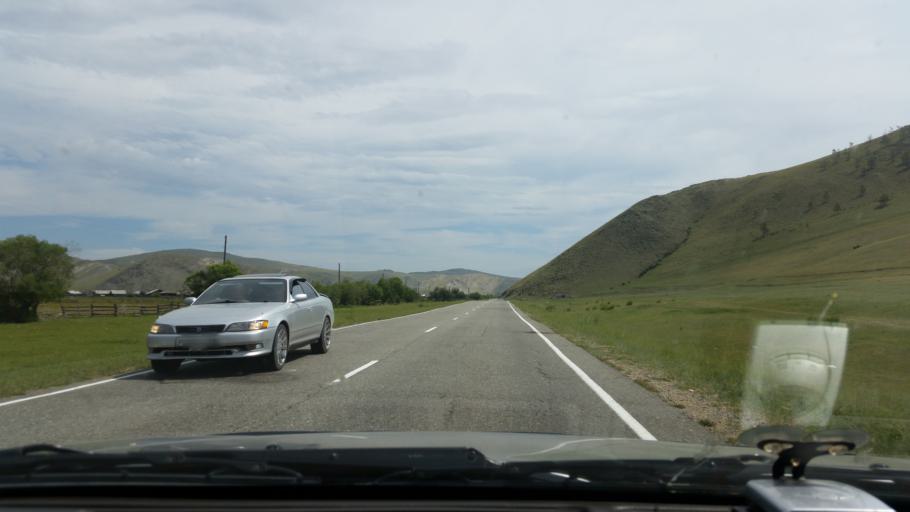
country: RU
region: Irkutsk
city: Yelantsy
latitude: 52.8062
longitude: 106.4540
